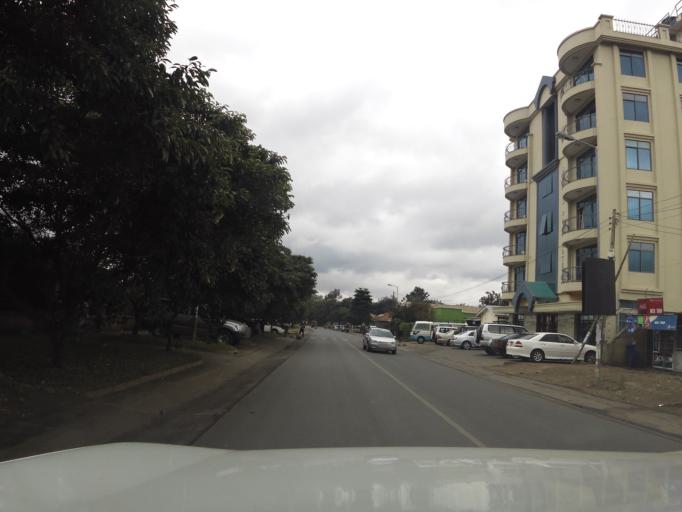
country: TZ
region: Arusha
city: Arusha
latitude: -3.3657
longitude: 36.6830
